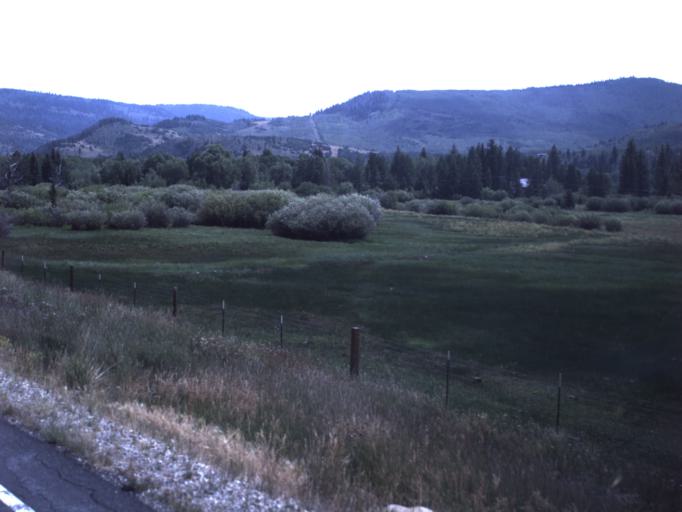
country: US
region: Utah
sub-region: Summit County
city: Francis
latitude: 40.5532
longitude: -111.1512
